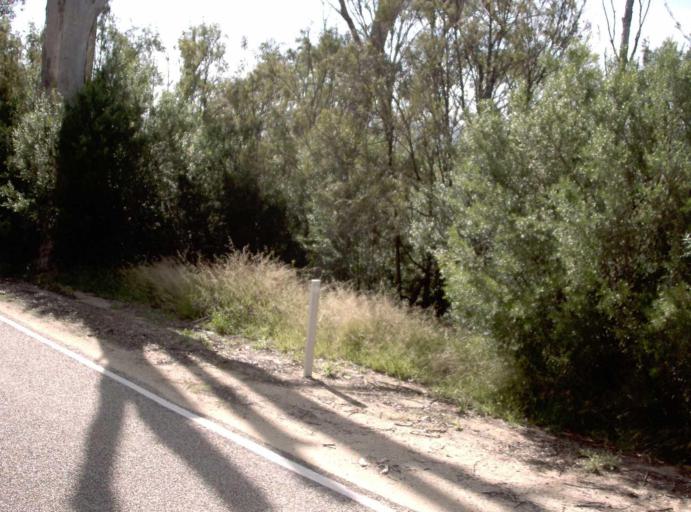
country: AU
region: Victoria
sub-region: East Gippsland
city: Lakes Entrance
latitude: -37.5161
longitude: 148.1641
